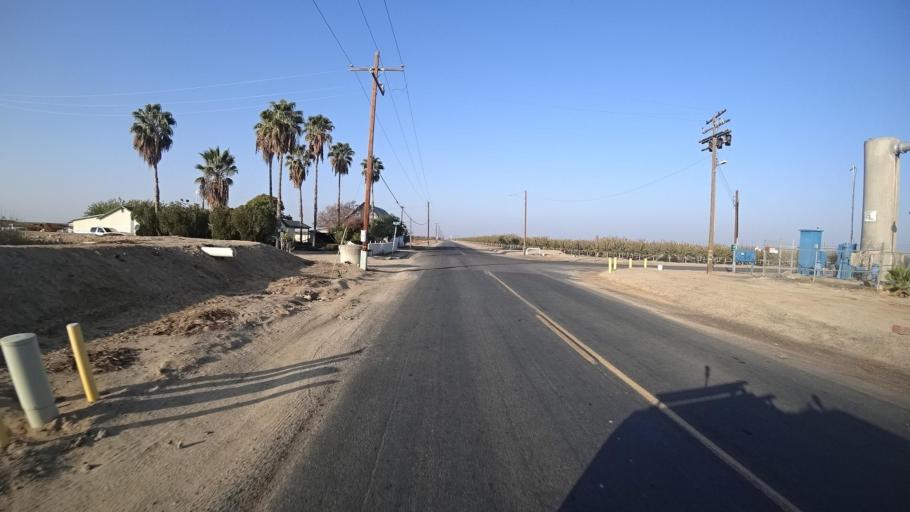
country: US
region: California
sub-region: Tulare County
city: Richgrove
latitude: 35.7907
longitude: -119.1429
